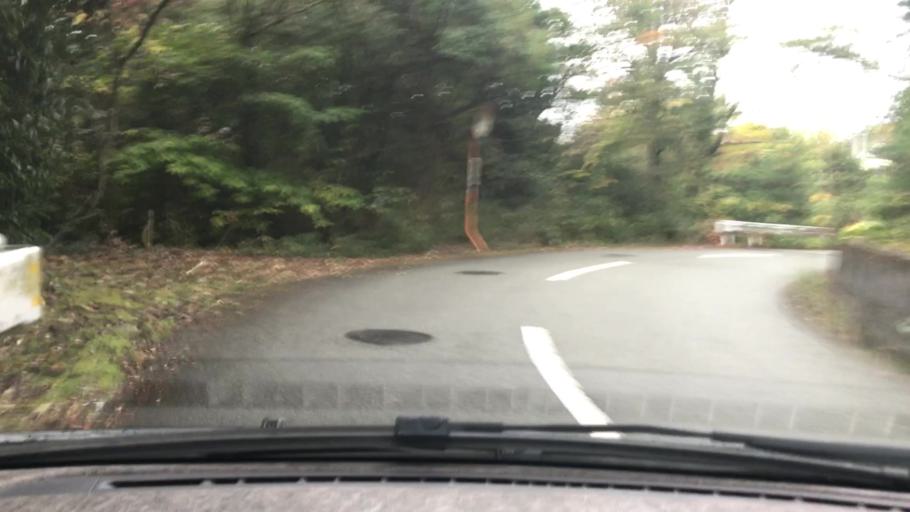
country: JP
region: Hyogo
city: Takarazuka
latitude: 34.8327
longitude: 135.2974
